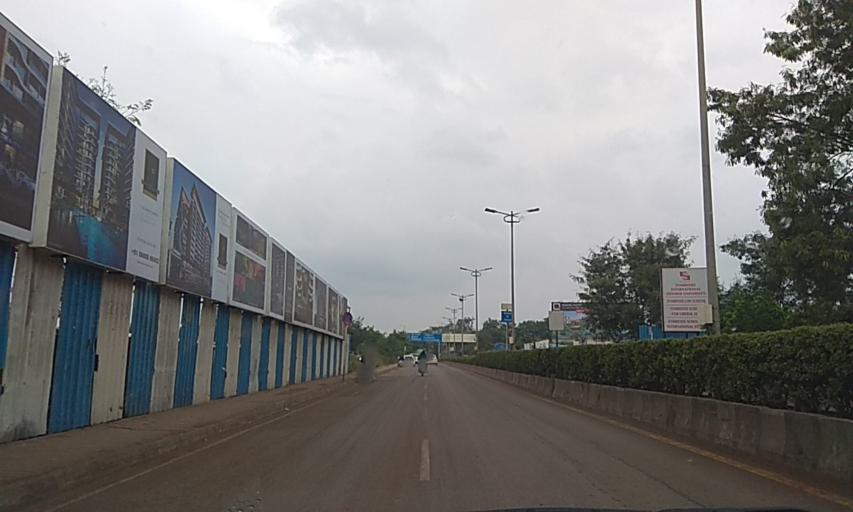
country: IN
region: Maharashtra
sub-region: Pune Division
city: Lohogaon
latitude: 18.5759
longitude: 73.9077
